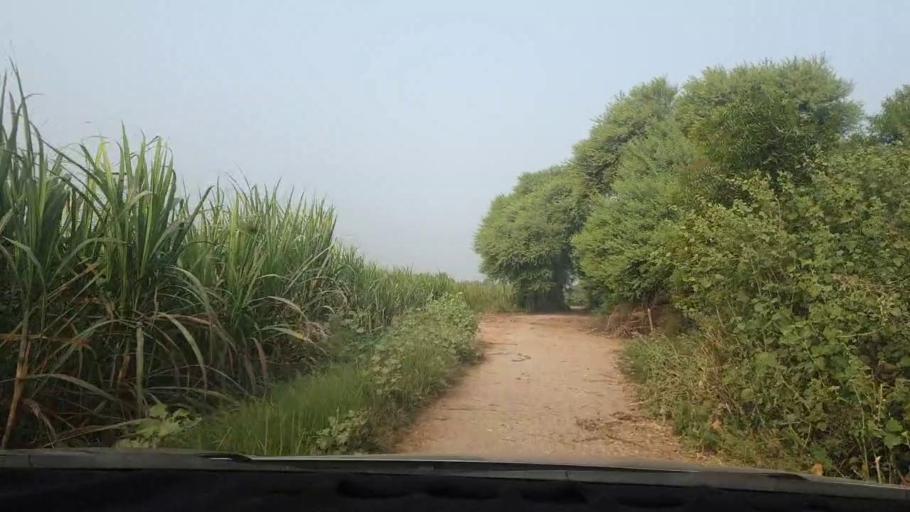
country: PK
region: Sindh
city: Matiari
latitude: 25.6012
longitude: 68.5506
